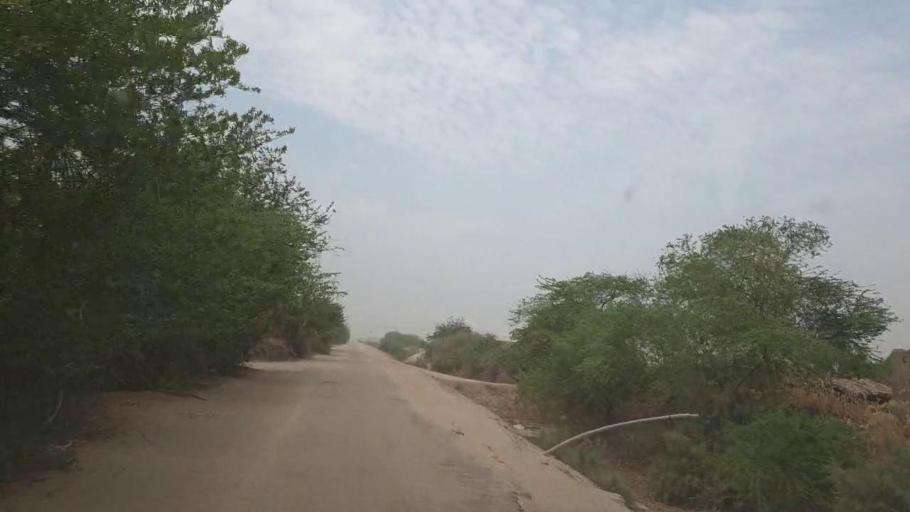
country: PK
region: Sindh
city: Kot Diji
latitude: 27.4411
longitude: 68.7148
